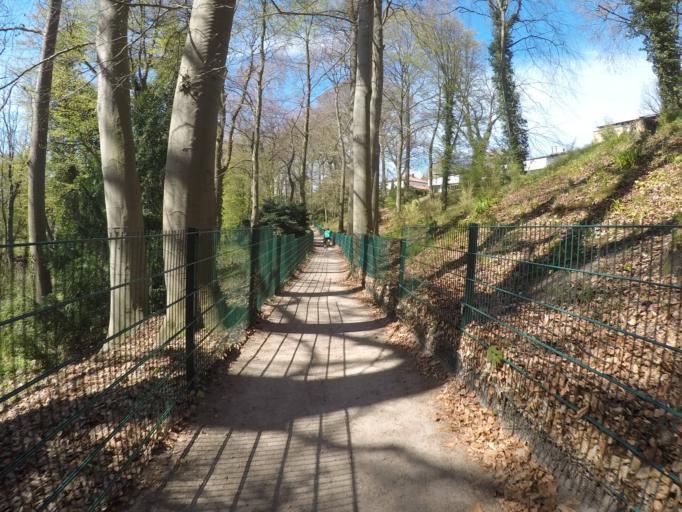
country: DE
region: Hamburg
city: Lemsahl-Mellingstedt
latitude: 53.6723
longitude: 10.0965
